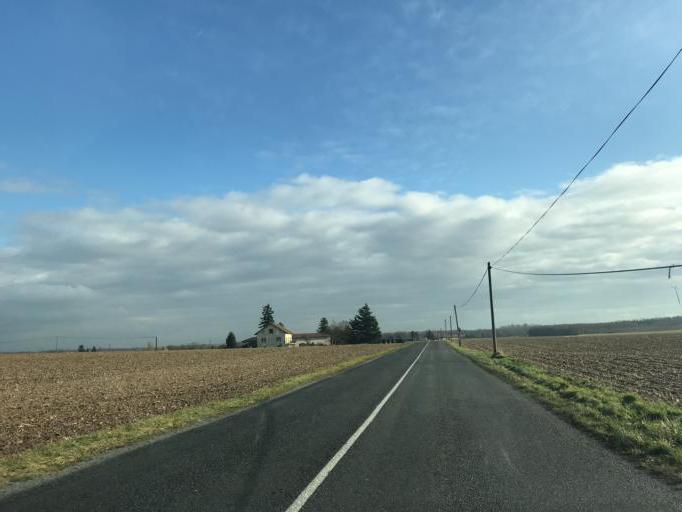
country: FR
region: Rhone-Alpes
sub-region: Departement de l'Ain
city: Civrieux
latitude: 45.9335
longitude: 4.8910
